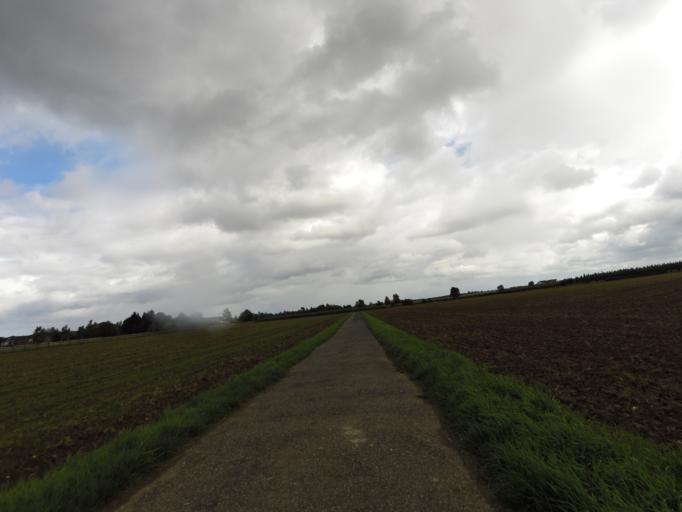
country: DE
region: North Rhine-Westphalia
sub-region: Regierungsbezirk Koln
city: Rheinbach
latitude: 50.6160
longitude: 6.9560
